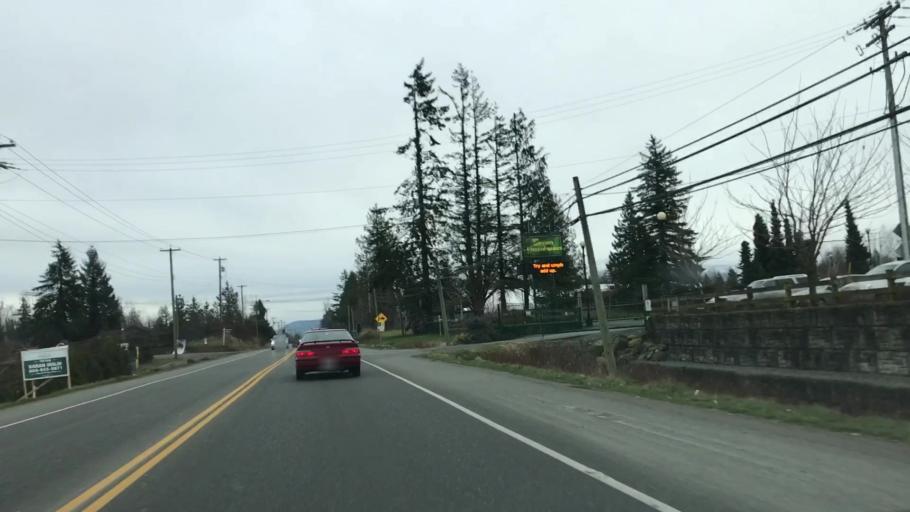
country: CA
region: British Columbia
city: Aldergrove
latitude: 49.0571
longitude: -122.4226
